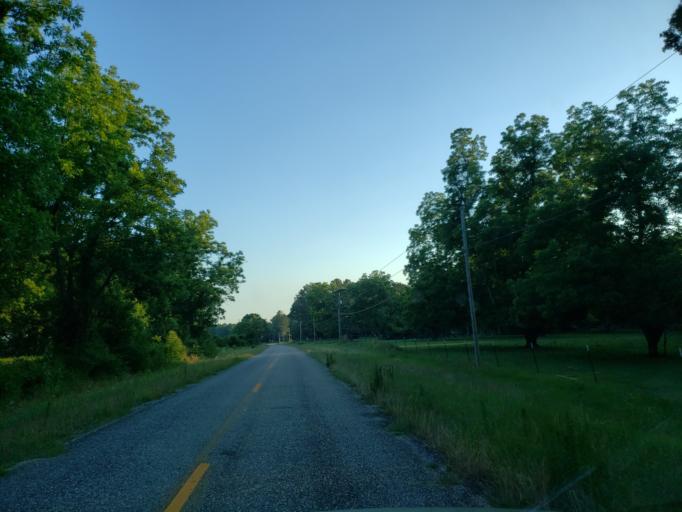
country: US
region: Georgia
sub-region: Crisp County
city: Cordele
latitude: 32.0243
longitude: -83.7496
